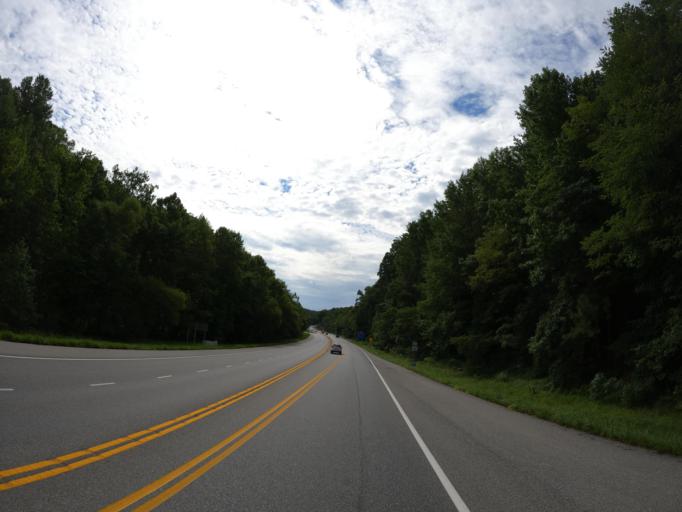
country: US
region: Maryland
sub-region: Saint Mary's County
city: Leonardtown
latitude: 38.2873
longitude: -76.6226
